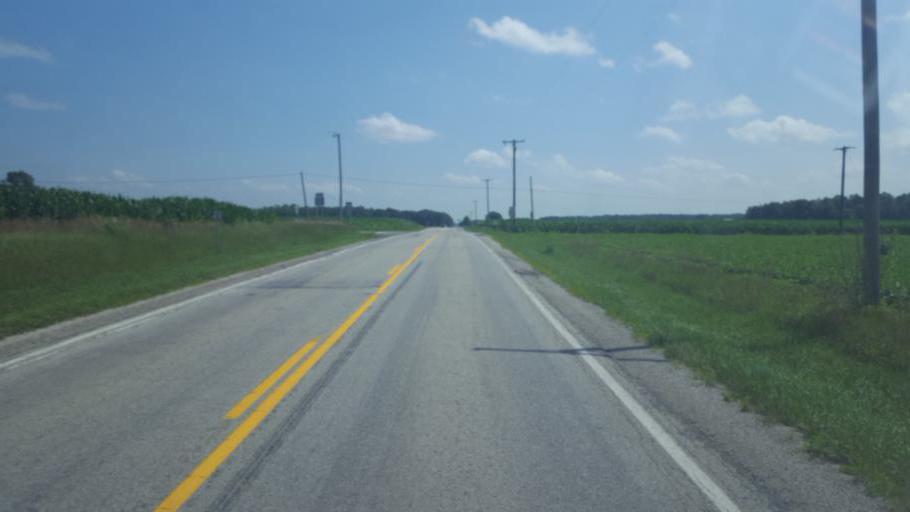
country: US
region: Ohio
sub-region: Huron County
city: Bellevue
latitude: 41.2032
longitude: -82.8379
